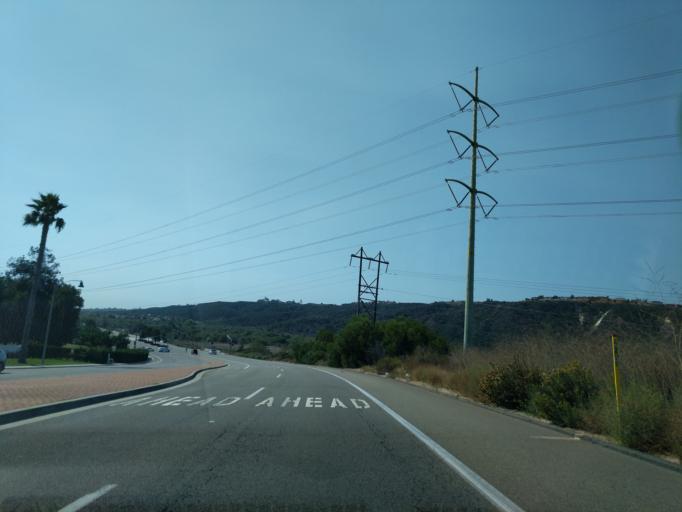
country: US
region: California
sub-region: San Diego County
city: Encinitas
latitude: 33.0913
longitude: -117.2692
